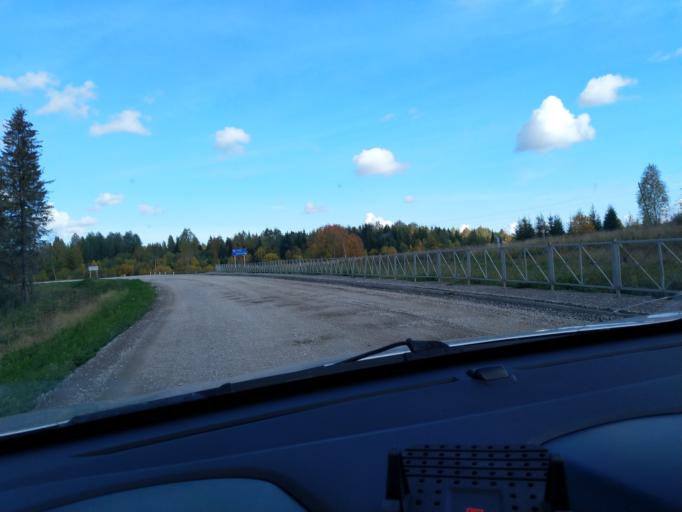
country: RU
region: Perm
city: Usol'ye
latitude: 59.4634
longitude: 56.3678
